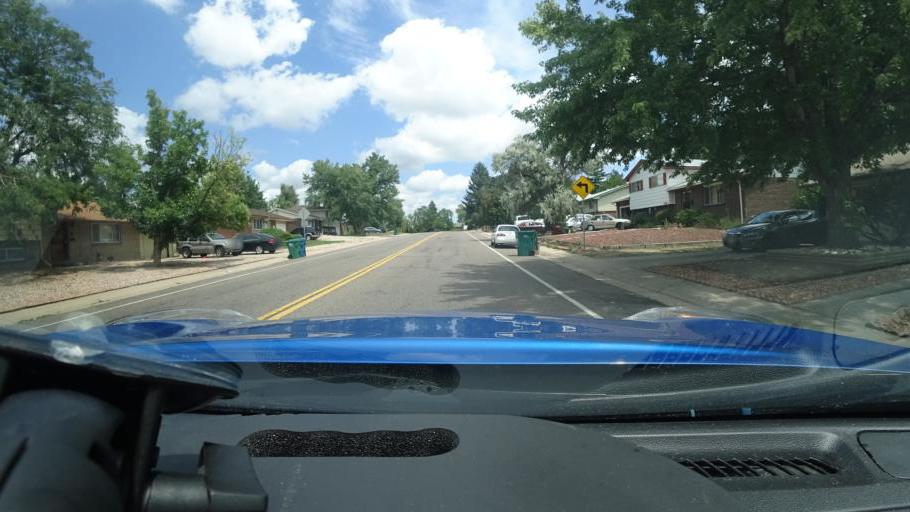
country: US
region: Colorado
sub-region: Adams County
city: Aurora
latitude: 39.6981
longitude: -104.8322
